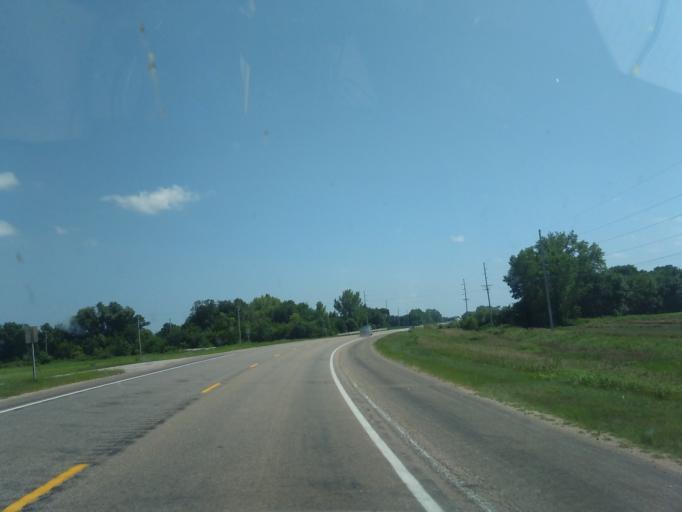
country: US
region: Nebraska
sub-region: Phelps County
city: Holdrege
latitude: 40.7105
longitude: -99.3794
